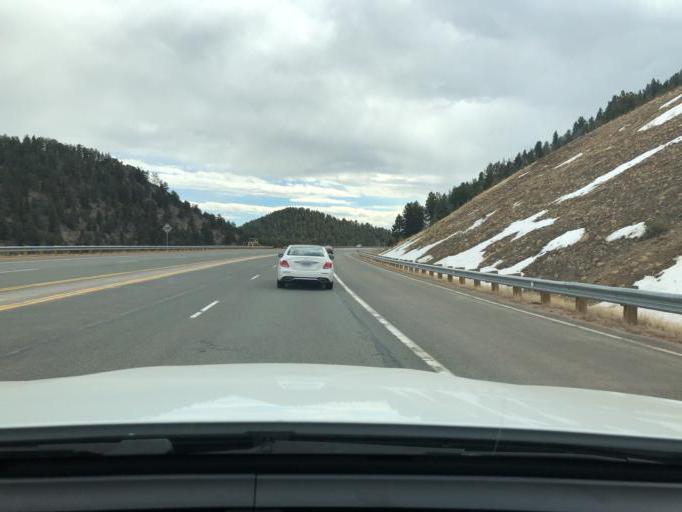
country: US
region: Colorado
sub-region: Gilpin County
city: Central City
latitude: 39.7790
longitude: -105.4785
